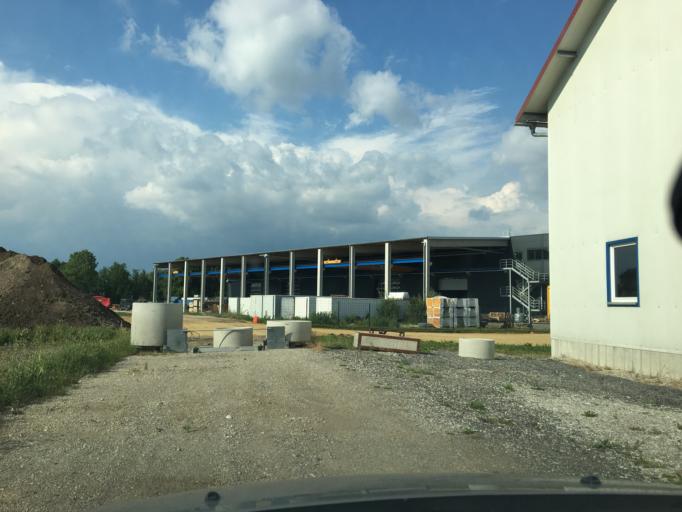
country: DE
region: Bavaria
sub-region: Lower Bavaria
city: Bruckberg
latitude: 48.4816
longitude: 12.0078
